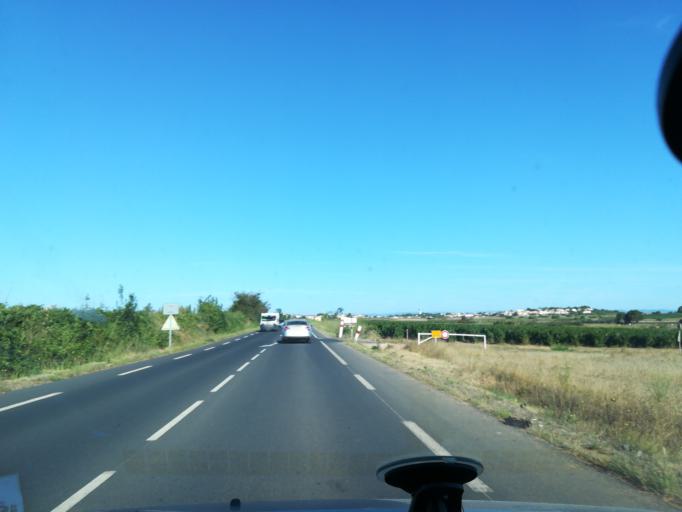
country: FR
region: Languedoc-Roussillon
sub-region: Departement de l'Herault
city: Portiragnes
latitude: 43.2942
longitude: 3.3578
